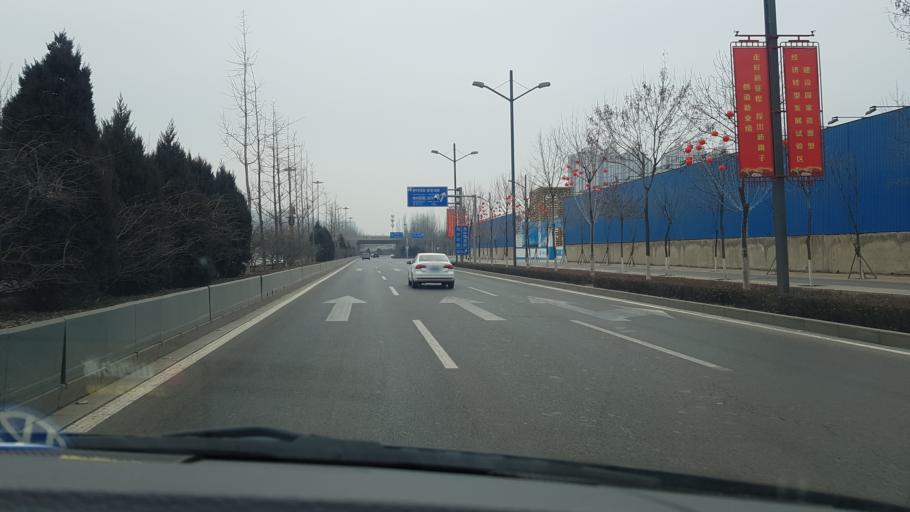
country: CN
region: Shanxi Sheng
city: Qianfeng
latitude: 37.7990
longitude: 112.5309
